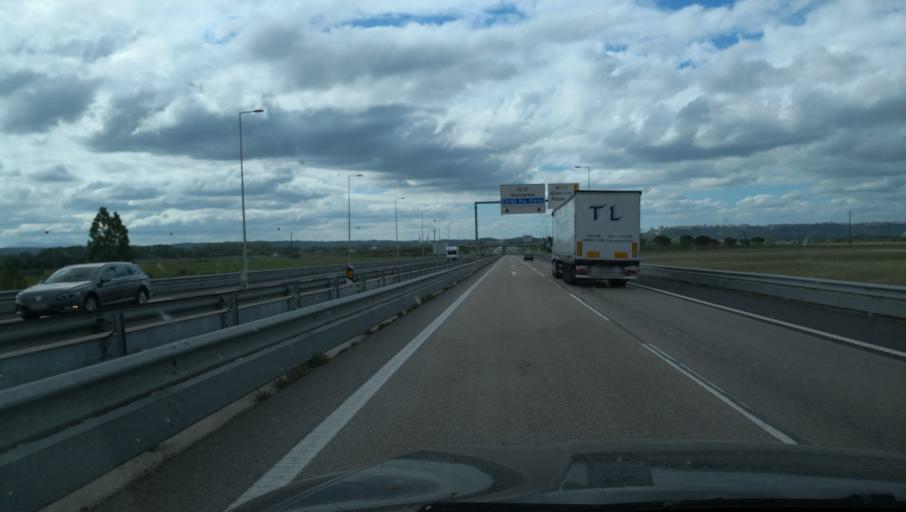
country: PT
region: Santarem
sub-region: Almeirim
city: Almeirim
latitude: 39.1875
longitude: -8.6431
